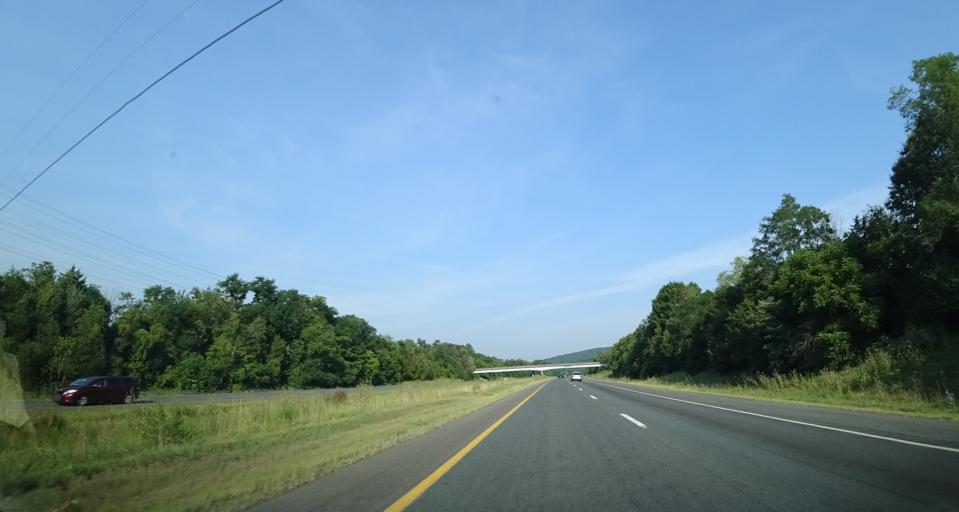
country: US
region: Virginia
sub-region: Prince William County
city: Haymarket
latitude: 38.8225
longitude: -77.6884
